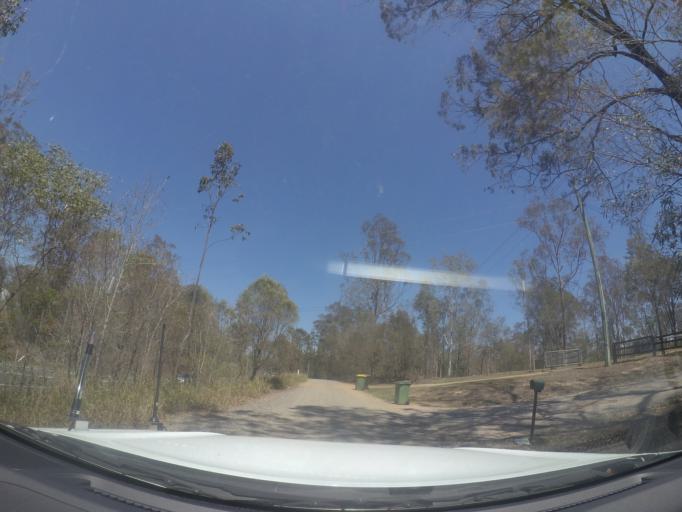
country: AU
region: Queensland
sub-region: Logan
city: North Maclean
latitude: -27.8064
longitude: 153.0473
